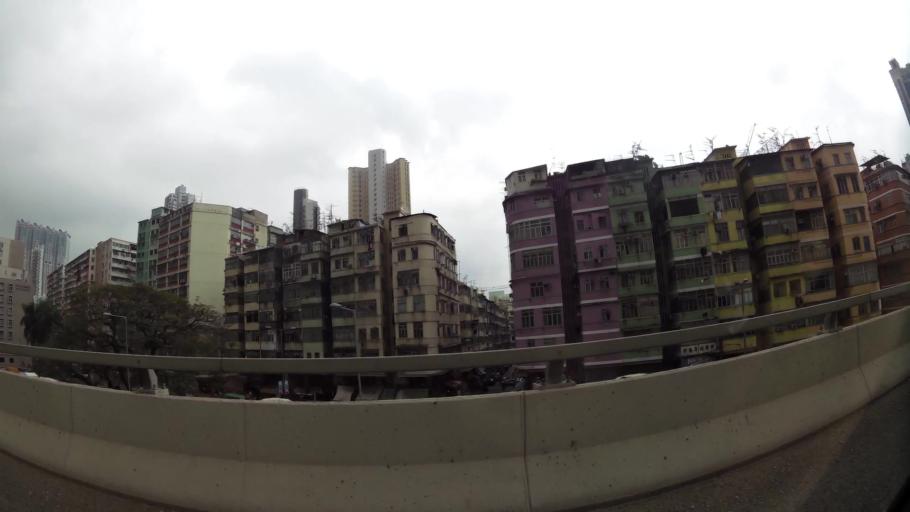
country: HK
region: Kowloon City
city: Kowloon
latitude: 22.3147
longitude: 114.1875
